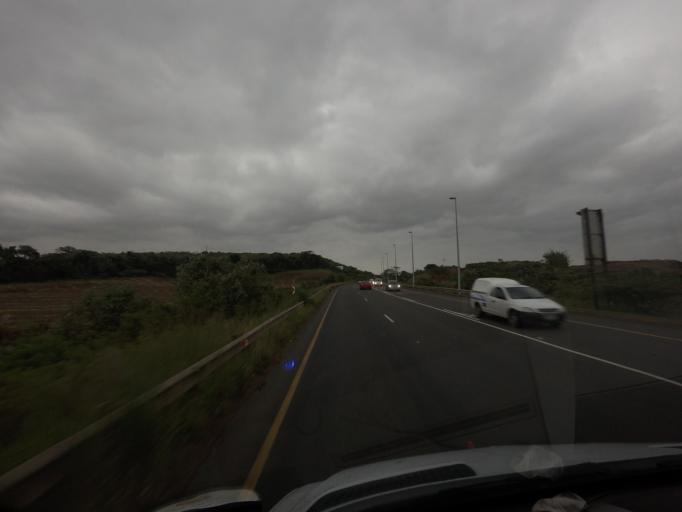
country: ZA
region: KwaZulu-Natal
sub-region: iLembe District Municipality
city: Ballitoville
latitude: -29.5609
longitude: 31.1824
